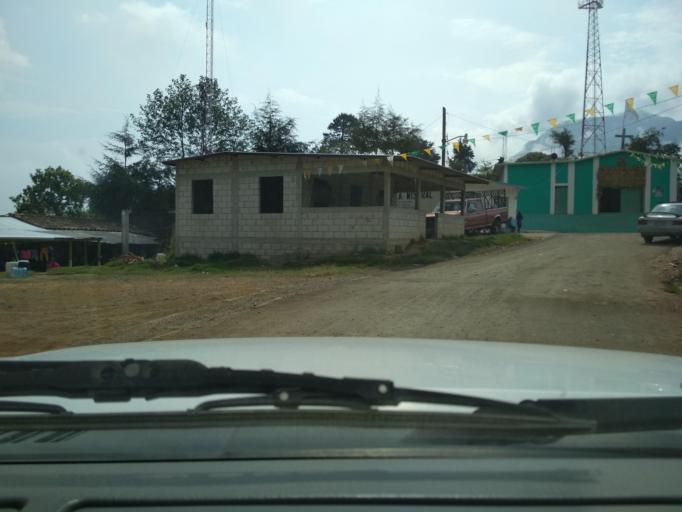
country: MX
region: Veracruz
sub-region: Camerino Z. Mendoza
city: Necoxtla
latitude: 18.7670
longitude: -97.1469
